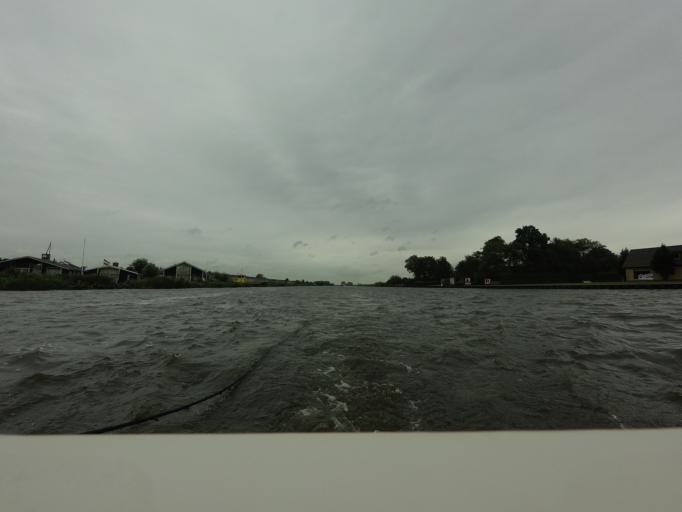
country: NL
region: Friesland
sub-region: Gemeente Boarnsterhim
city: Grou
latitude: 53.0996
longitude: 5.8492
